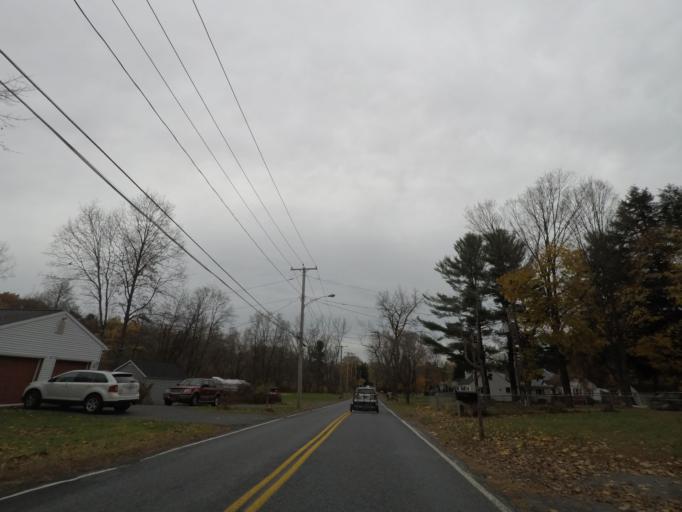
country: US
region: New York
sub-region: Rensselaer County
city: Wynantskill
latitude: 42.7275
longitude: -73.6564
